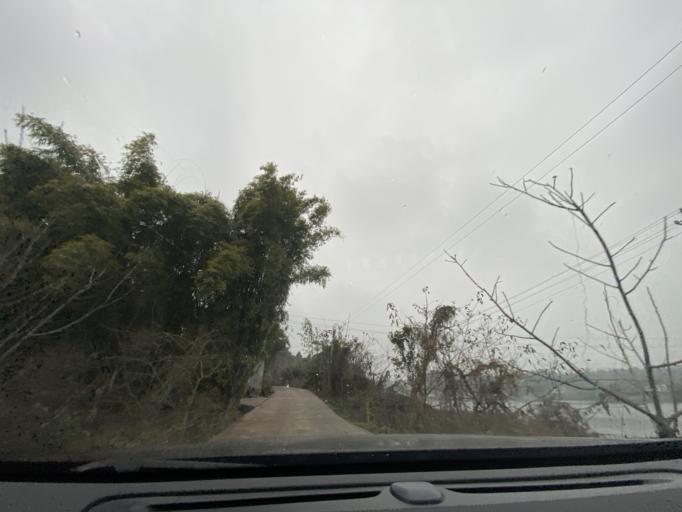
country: CN
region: Sichuan
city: Jiancheng
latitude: 30.3964
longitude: 104.6308
